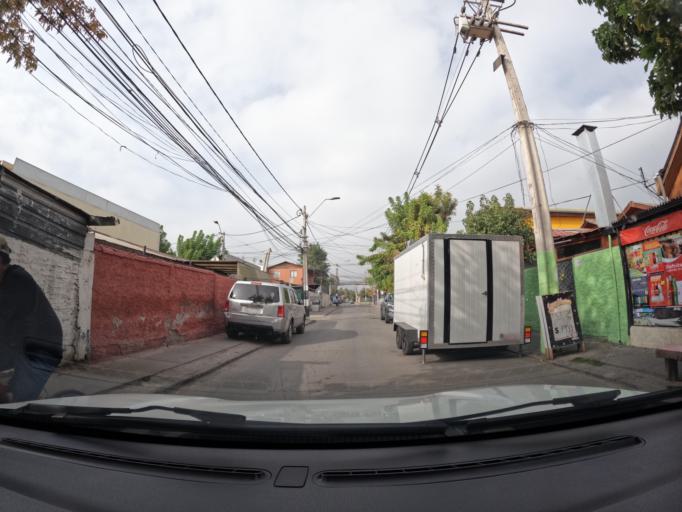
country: CL
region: Santiago Metropolitan
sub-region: Provincia de Santiago
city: Villa Presidente Frei, Nunoa, Santiago, Chile
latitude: -33.4699
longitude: -70.5472
